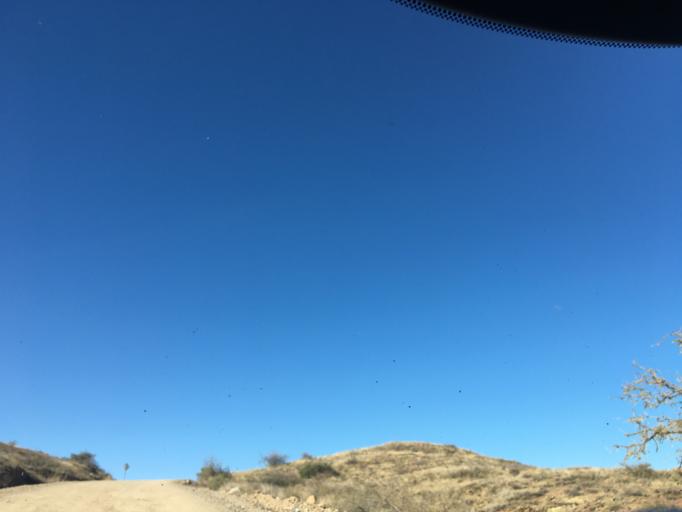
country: US
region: Arizona
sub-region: Yavapai County
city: Cordes Lakes
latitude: 34.2702
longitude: -112.1080
